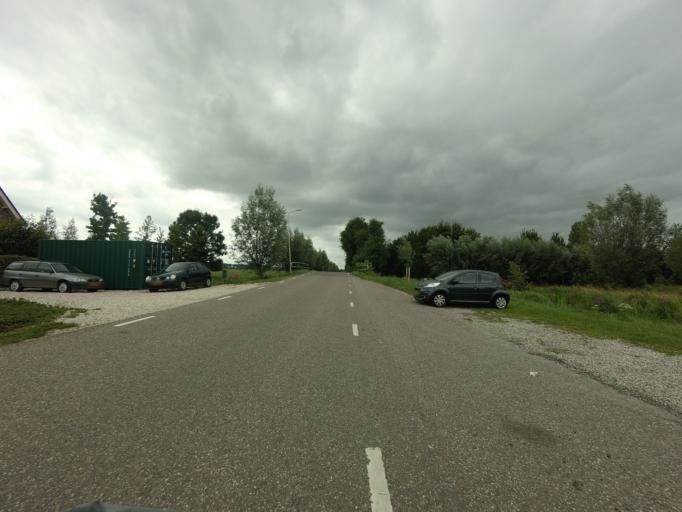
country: NL
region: South Holland
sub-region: Gemeente Giessenlanden
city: Giessenburg
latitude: 51.9018
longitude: 4.8998
